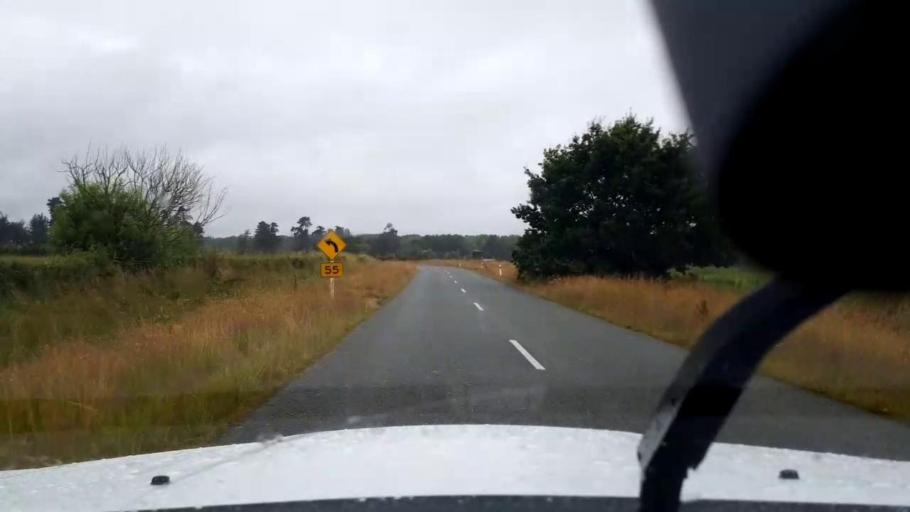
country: NZ
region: Canterbury
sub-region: Timaru District
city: Pleasant Point
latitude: -44.2535
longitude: 171.2385
